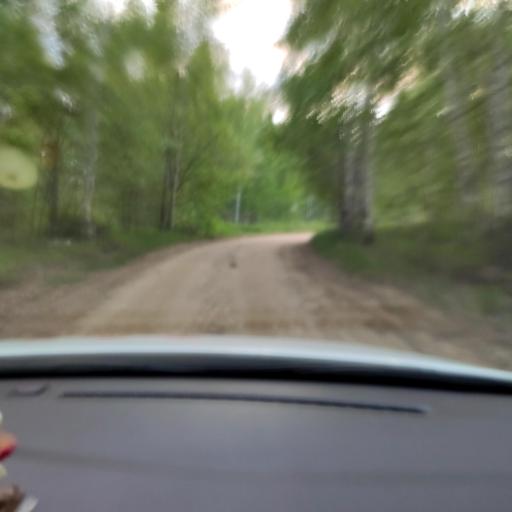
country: RU
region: Tatarstan
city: Stolbishchi
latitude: 55.5921
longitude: 49.0981
